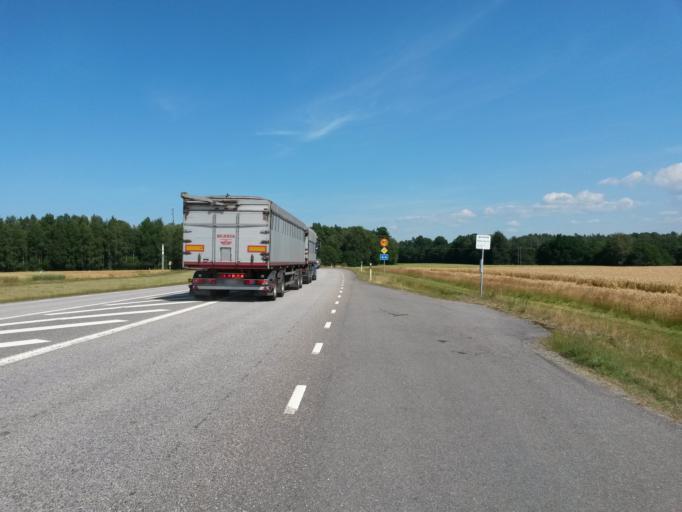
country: SE
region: Vaestra Goetaland
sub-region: Lidkopings Kommun
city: Lidkoping
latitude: 58.4846
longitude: 13.1236
